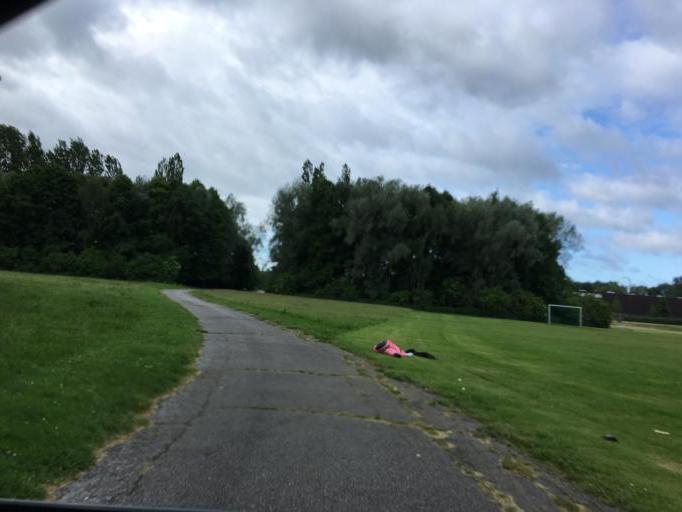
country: SE
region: Skane
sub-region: Burlovs Kommun
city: Arloev
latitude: 55.5744
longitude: 13.0531
